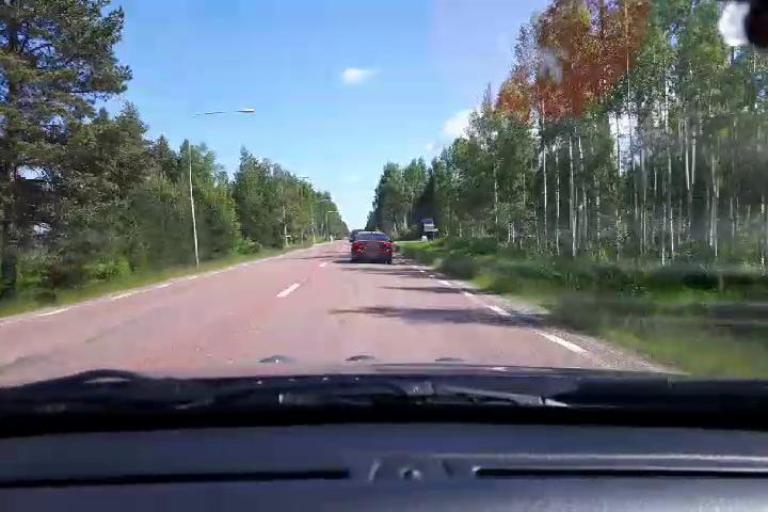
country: SE
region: Gaevleborg
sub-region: Hudiksvalls Kommun
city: Delsbo
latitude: 61.7958
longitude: 16.5723
